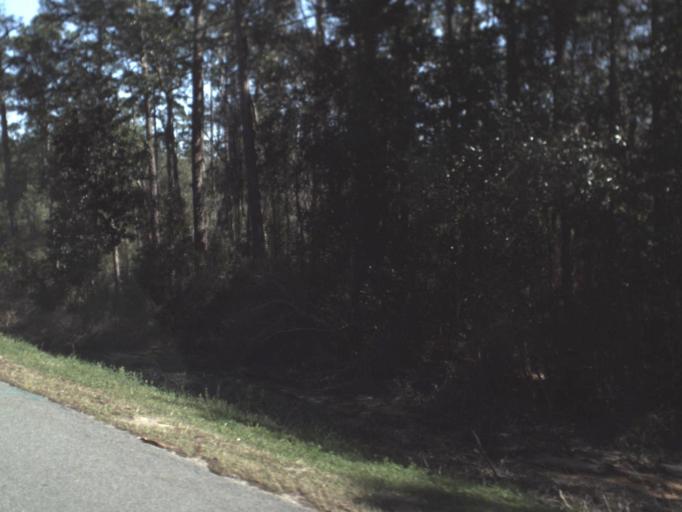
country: US
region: Florida
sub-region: Bay County
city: Laguna Beach
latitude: 30.3130
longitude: -85.8125
